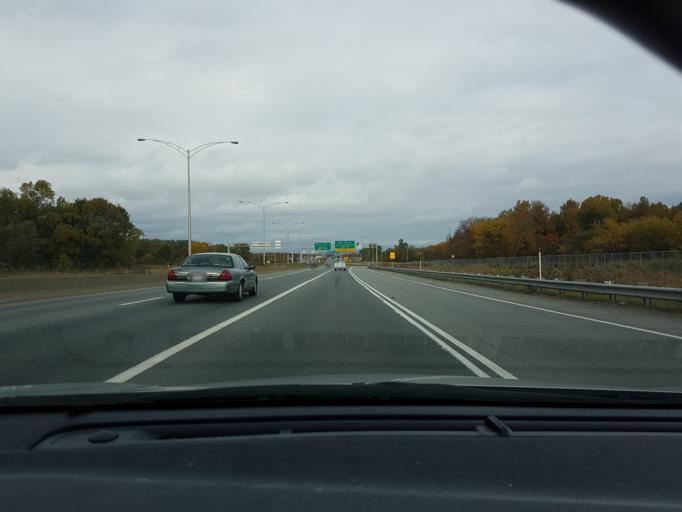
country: CA
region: Quebec
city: L'Ancienne-Lorette
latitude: 46.8192
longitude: -71.2934
